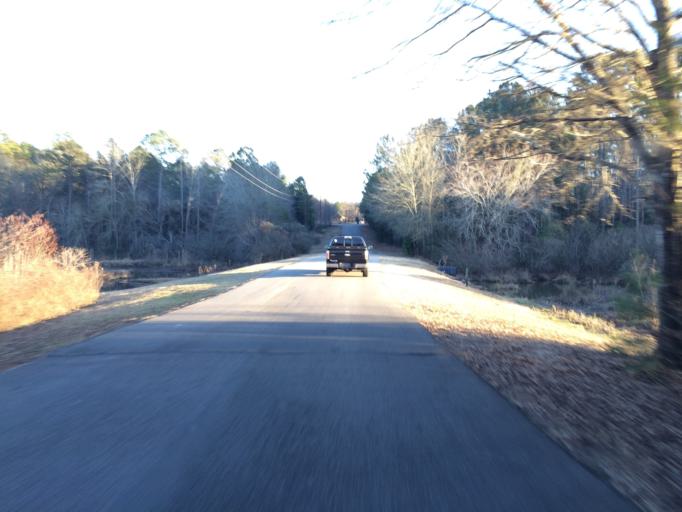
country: US
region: Texas
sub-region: Wood County
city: Hawkins
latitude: 32.7232
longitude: -95.1761
